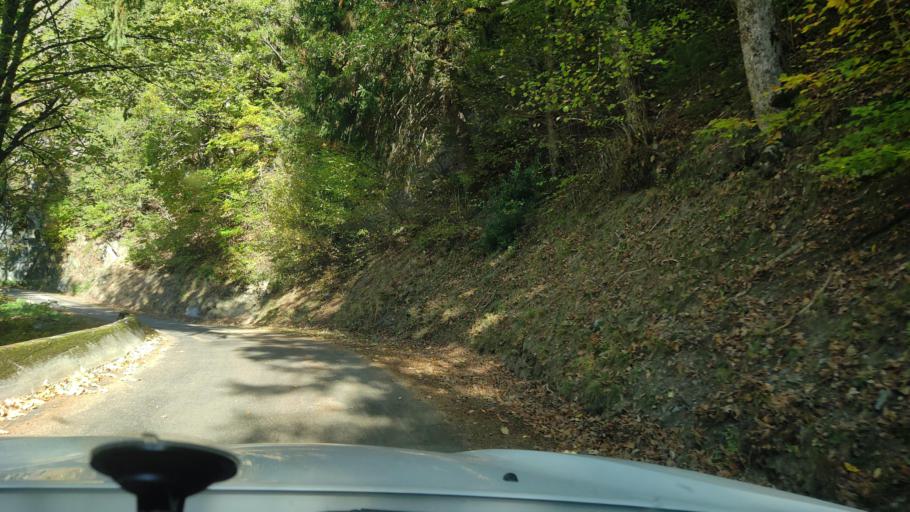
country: FR
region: Rhone-Alpes
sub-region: Departement de la Savoie
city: Beaufort
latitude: 45.7257
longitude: 6.5058
